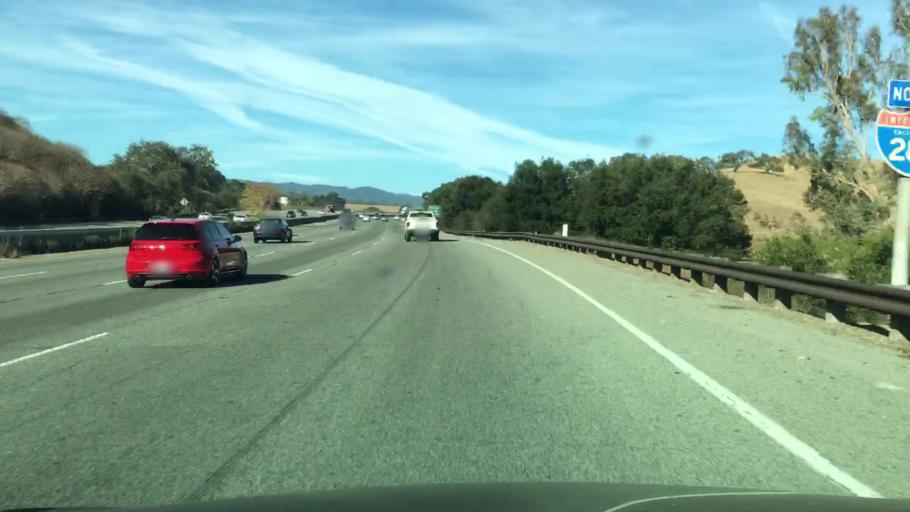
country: US
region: California
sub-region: San Mateo County
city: Ladera
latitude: 37.3923
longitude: -122.1686
